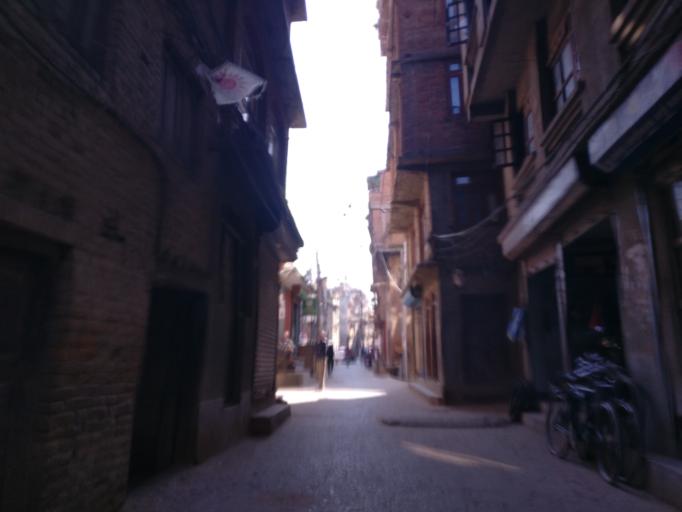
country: NP
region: Central Region
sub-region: Bagmati Zone
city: Patan
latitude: 27.6735
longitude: 85.3278
